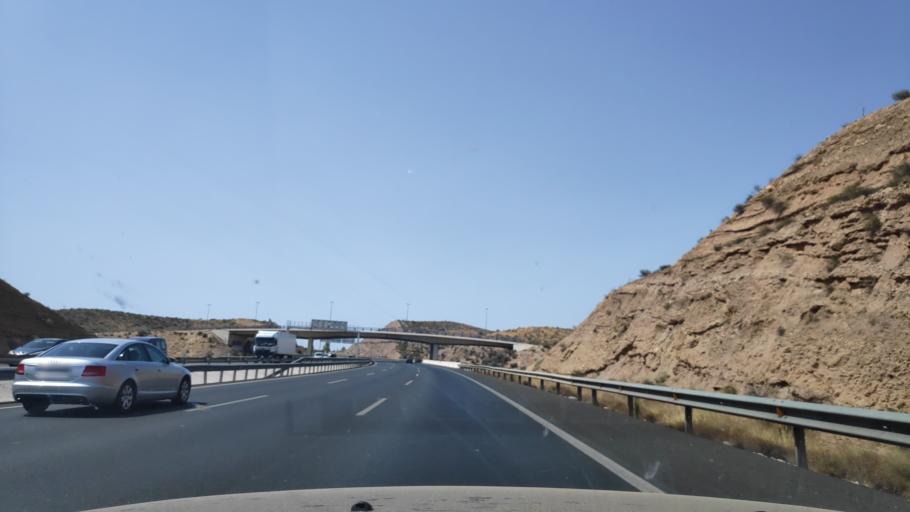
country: ES
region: Murcia
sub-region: Murcia
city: Molina de Segura
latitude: 38.0395
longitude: -1.1611
